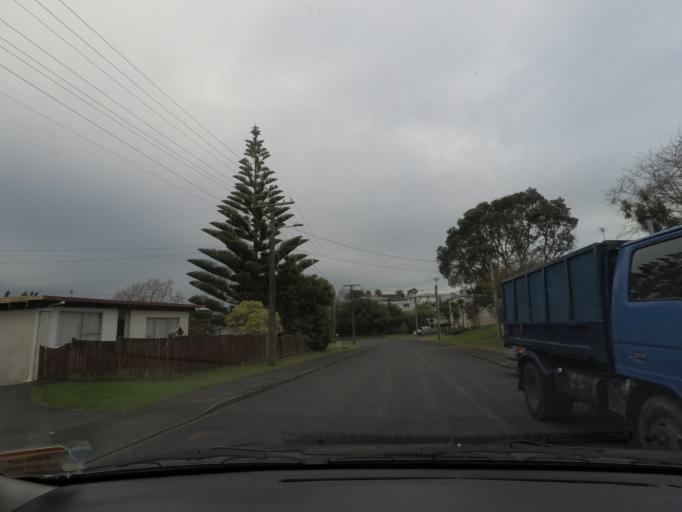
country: NZ
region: Auckland
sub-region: Auckland
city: Rosebank
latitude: -36.8616
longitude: 174.6422
